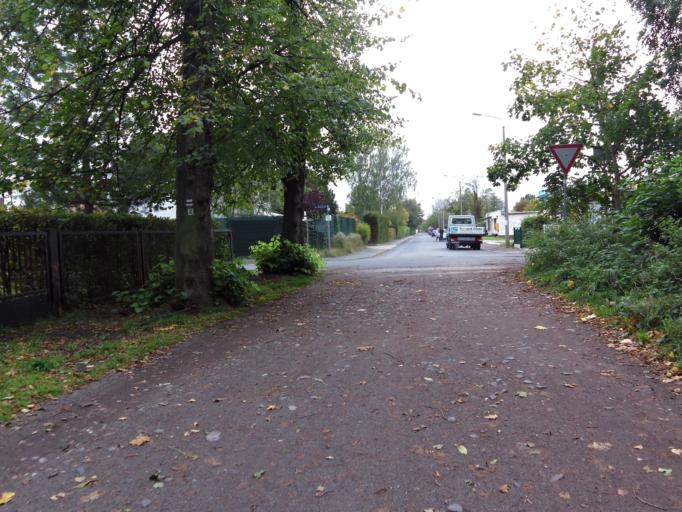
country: DE
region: Saxony
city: Markkleeberg
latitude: 51.2929
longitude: 12.3595
